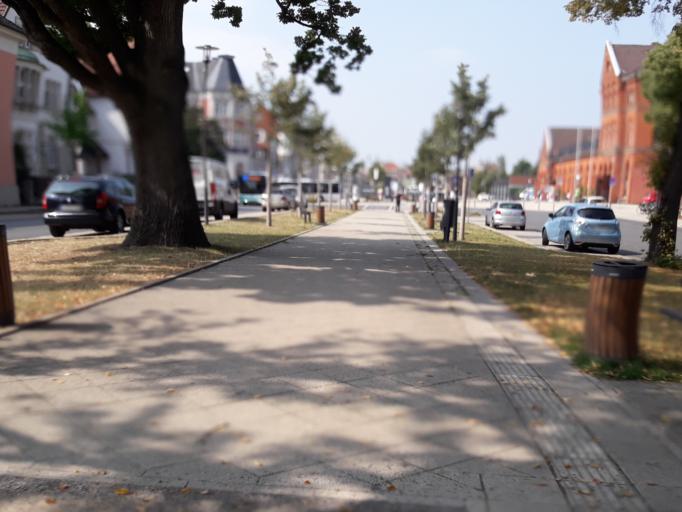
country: DE
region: North Rhine-Westphalia
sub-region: Regierungsbezirk Detmold
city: Detmold
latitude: 51.9398
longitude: 8.8746
